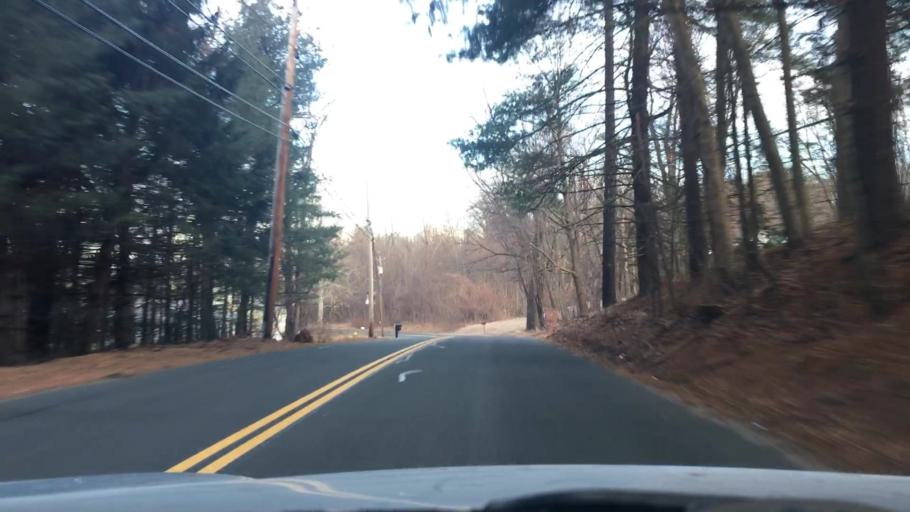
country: US
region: Massachusetts
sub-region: Hampden County
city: Westfield
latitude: 42.0931
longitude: -72.7113
